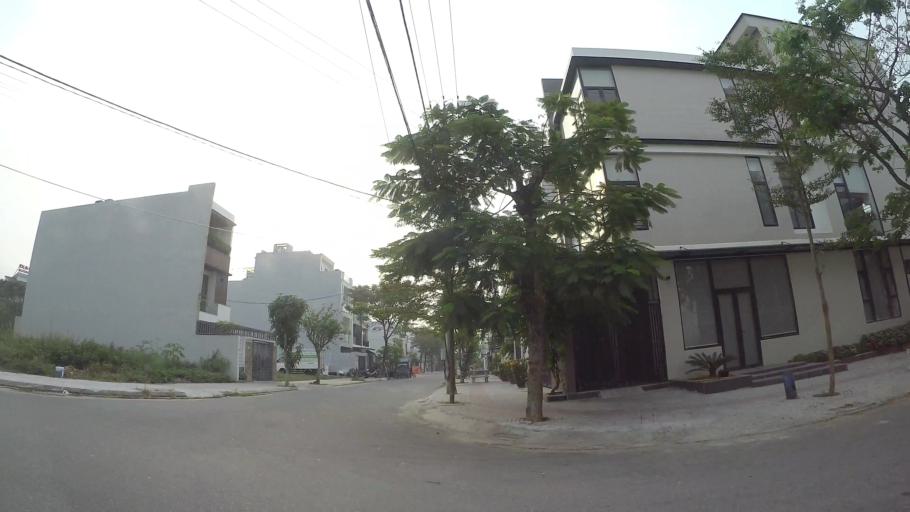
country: VN
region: Da Nang
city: Cam Le
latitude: 16.0213
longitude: 108.2276
